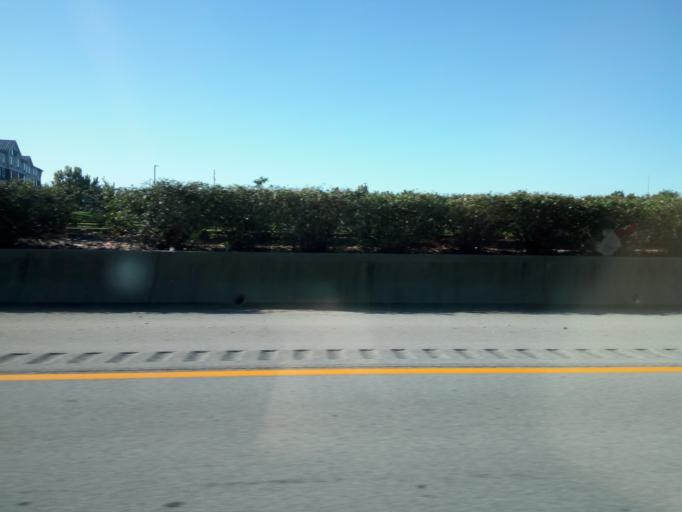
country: US
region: Kentucky
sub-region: Jefferson County
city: Douglass Hills
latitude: 38.2240
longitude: -85.5441
